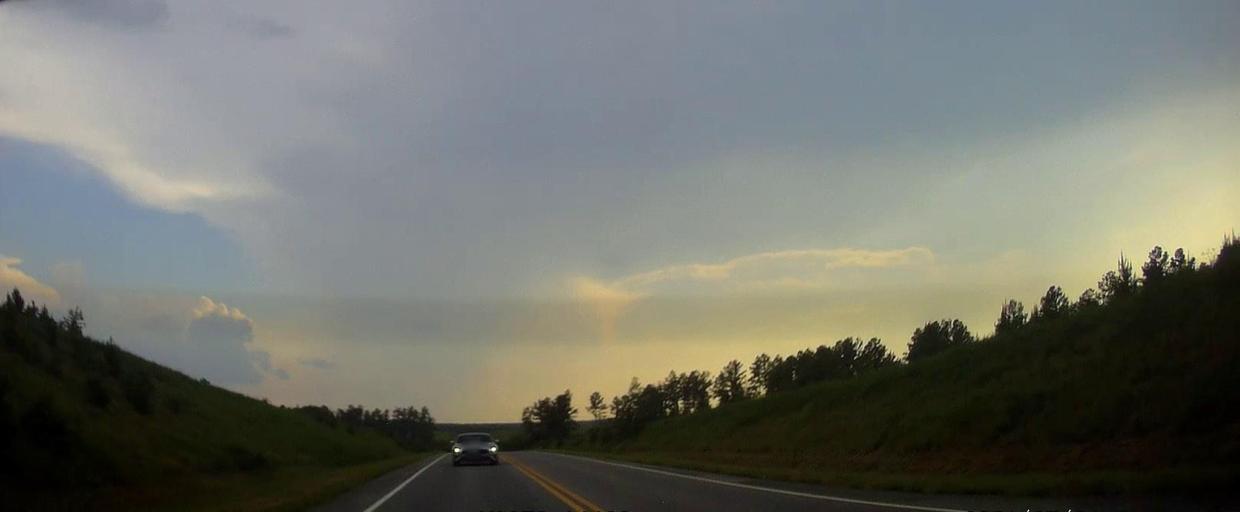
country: US
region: Georgia
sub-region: Laurens County
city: East Dublin
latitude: 32.6211
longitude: -82.8807
